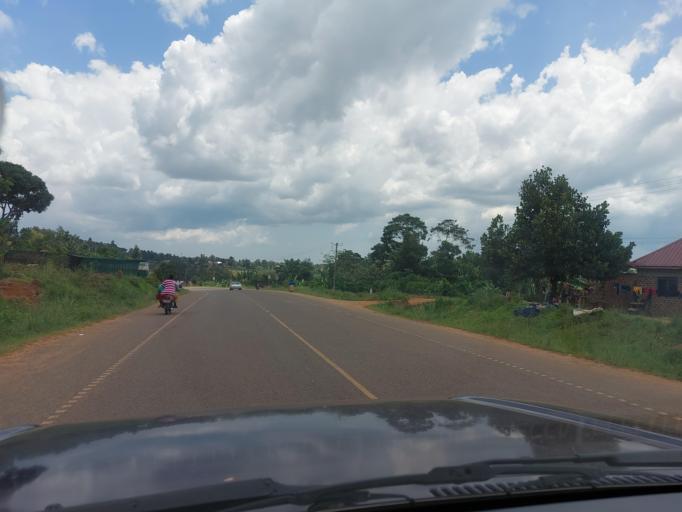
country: UG
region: Central Region
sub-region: Mukono District
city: Mukono
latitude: 0.3122
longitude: 32.7733
